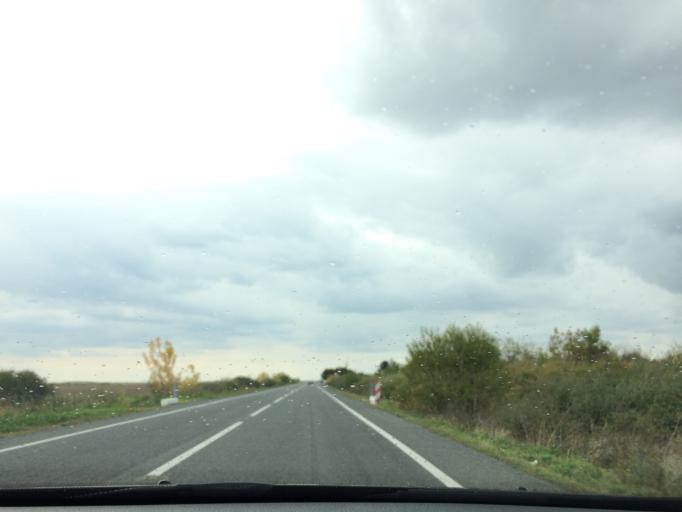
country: RO
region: Timis
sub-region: Oras Recas
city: Izvin
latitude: 45.7975
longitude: 21.4341
